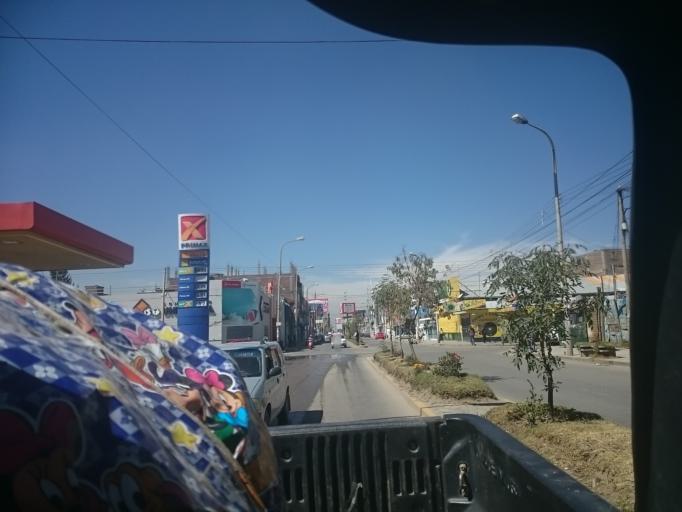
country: PE
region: Junin
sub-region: Provincia de Huancayo
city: El Tambo
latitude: -12.0517
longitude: -75.2208
